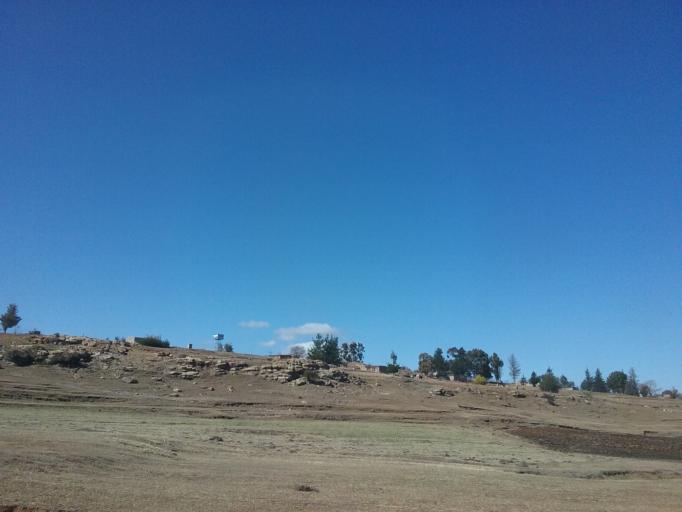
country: LS
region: Maseru
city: Maseru
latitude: -29.4690
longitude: 27.5775
